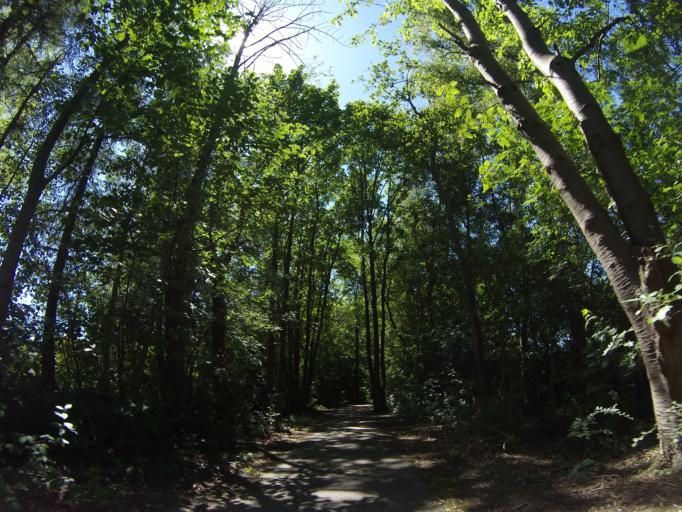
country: NL
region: Drenthe
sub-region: Gemeente Assen
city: Assen
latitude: 52.9744
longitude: 6.5650
